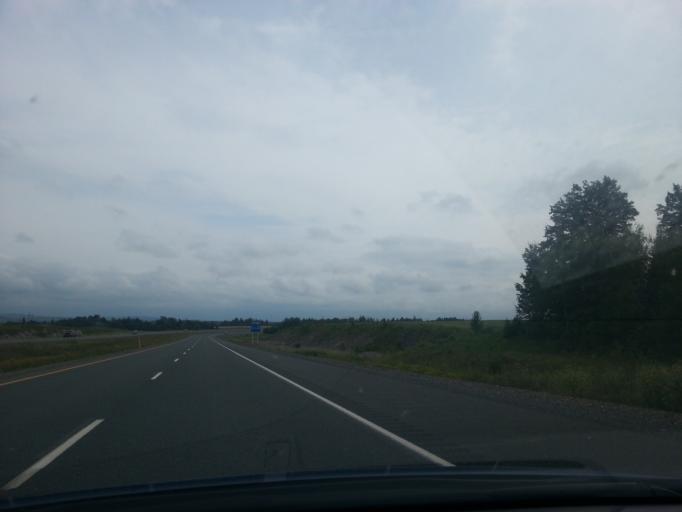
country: CA
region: New Brunswick
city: Florenceville-Bristol
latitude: 46.2151
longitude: -67.6030
